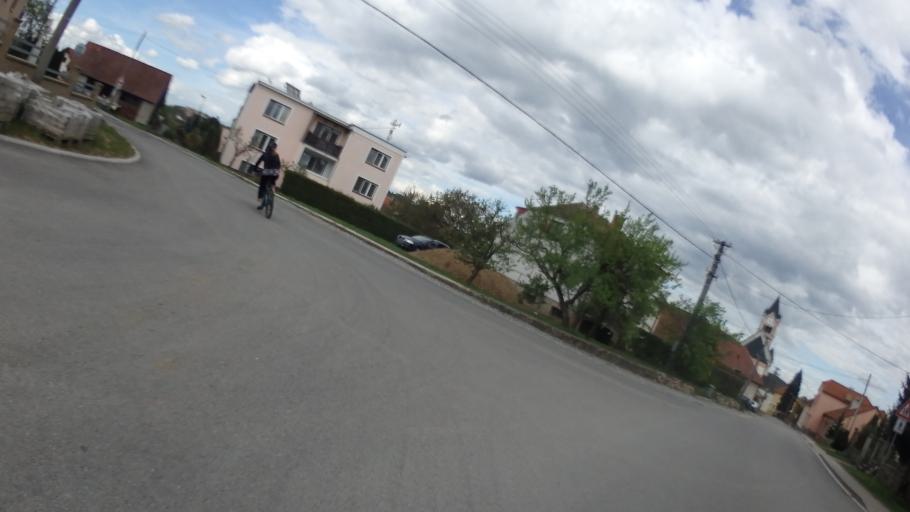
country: CZ
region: Vysocina
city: Merin
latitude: 49.3503
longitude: 15.9355
